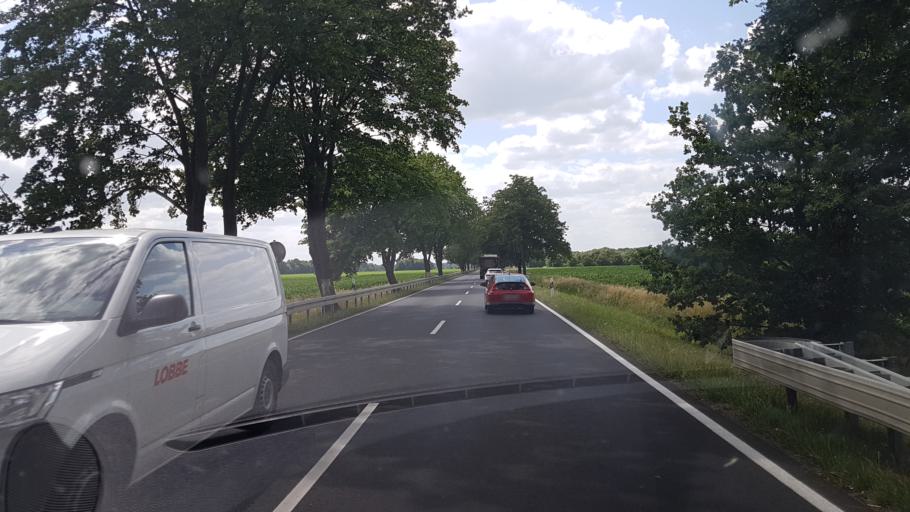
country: DE
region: Brandenburg
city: Lauchhammer
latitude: 51.4639
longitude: 13.7648
